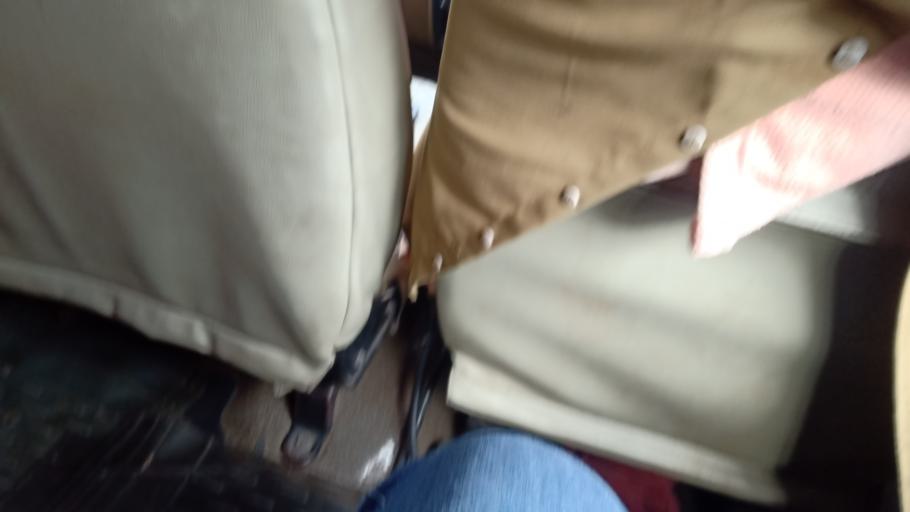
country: IN
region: Telangana
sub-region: Rangareddi
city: Kukatpalli
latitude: 17.4966
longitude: 78.4137
